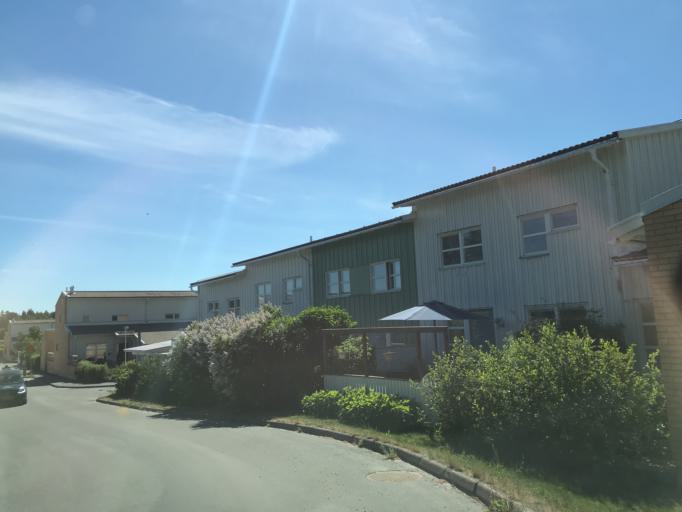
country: SE
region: Stockholm
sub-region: Upplands Vasby Kommun
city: Upplands Vaesby
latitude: 59.4637
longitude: 17.8934
